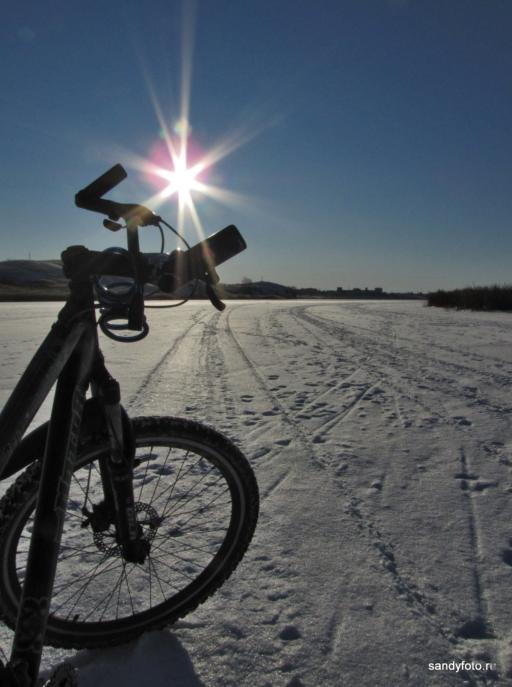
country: RU
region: Chelyabinsk
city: Troitsk
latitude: 54.0836
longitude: 61.5862
